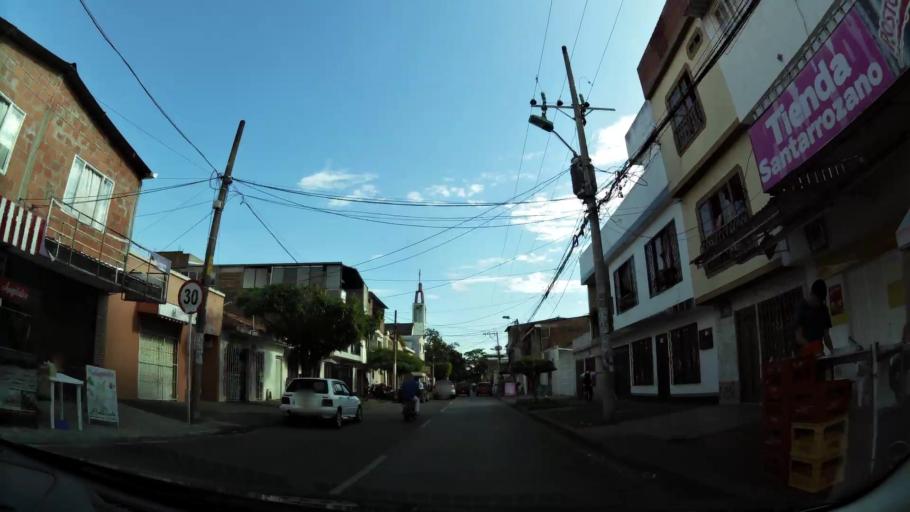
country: CO
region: Valle del Cauca
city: Cali
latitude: 3.4248
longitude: -76.5260
